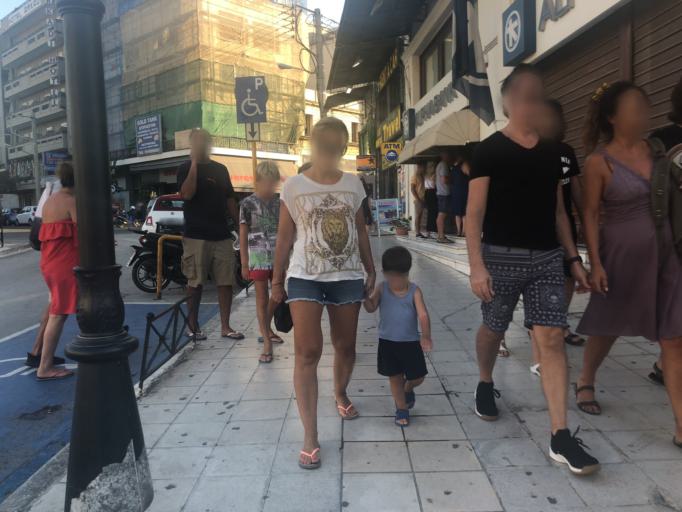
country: GR
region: Crete
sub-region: Nomos Chanias
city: Chania
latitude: 35.5140
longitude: 24.0173
